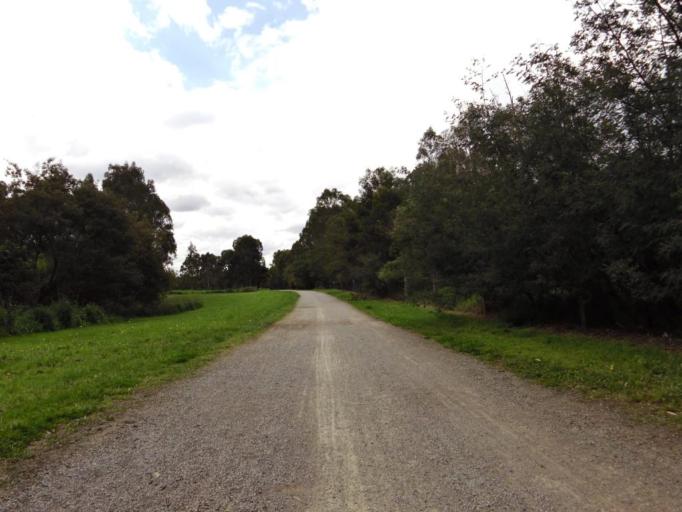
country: AU
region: Victoria
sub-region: Manningham
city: Bulleen
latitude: -37.7656
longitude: 145.0725
